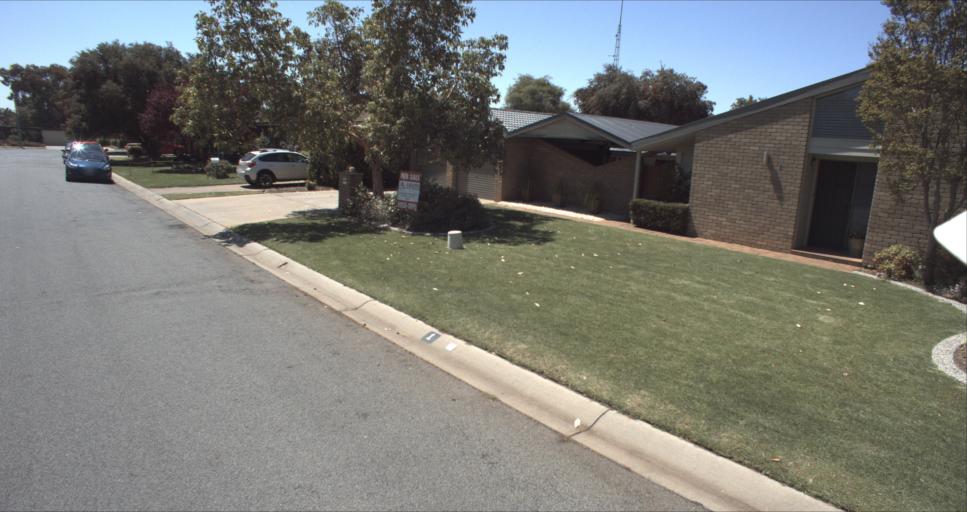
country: AU
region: New South Wales
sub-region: Leeton
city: Leeton
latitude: -34.5429
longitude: 146.4018
